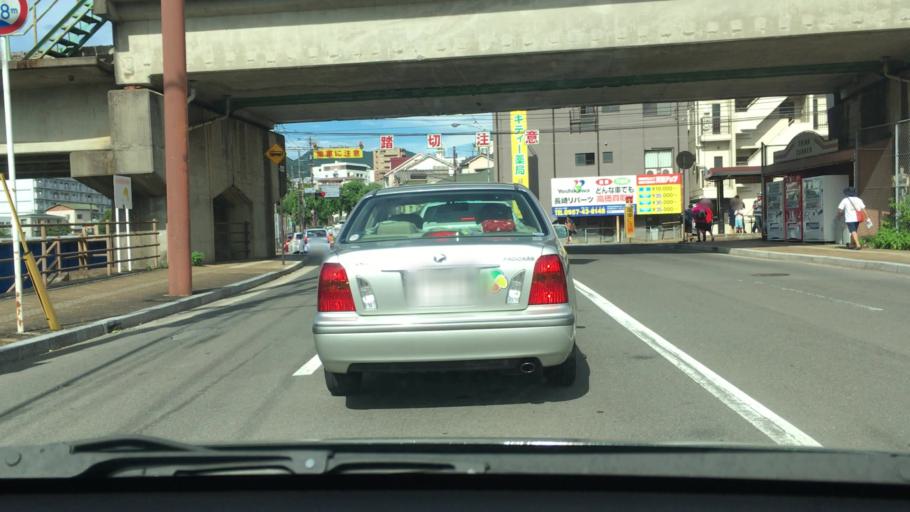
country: JP
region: Nagasaki
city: Nagasaki-shi
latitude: 32.7780
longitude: 129.8610
